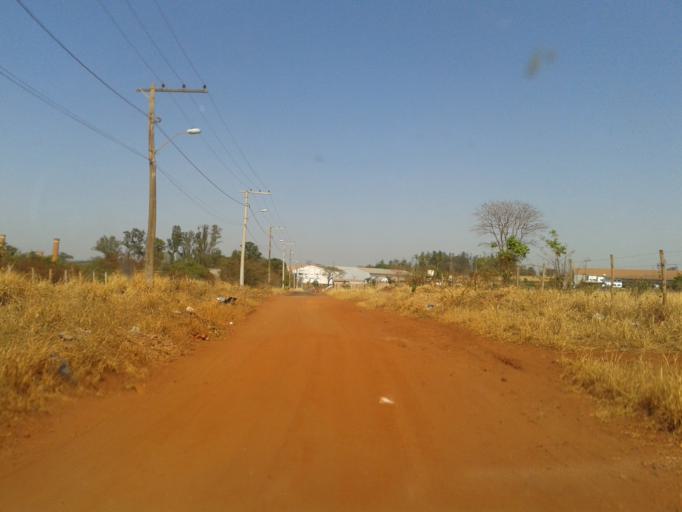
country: BR
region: Minas Gerais
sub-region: Ituiutaba
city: Ituiutaba
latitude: -18.9610
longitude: -49.4881
